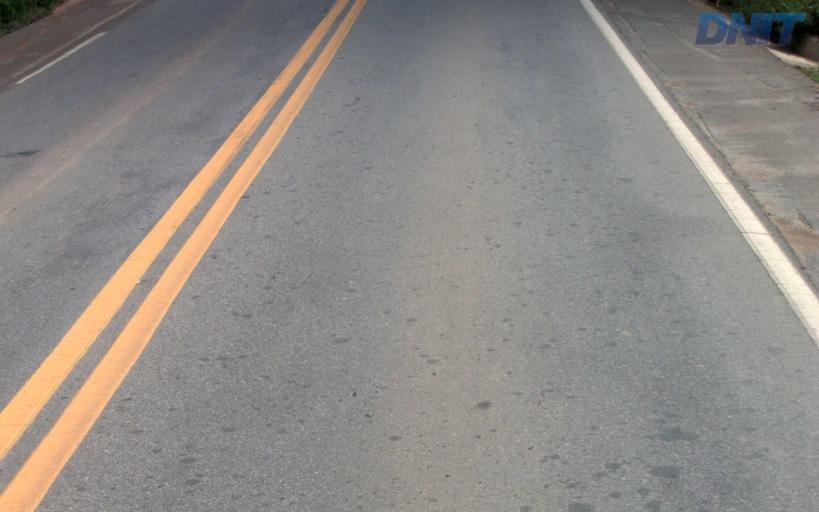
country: BR
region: Minas Gerais
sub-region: Belo Oriente
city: Belo Oriente
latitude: -19.1501
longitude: -42.2328
